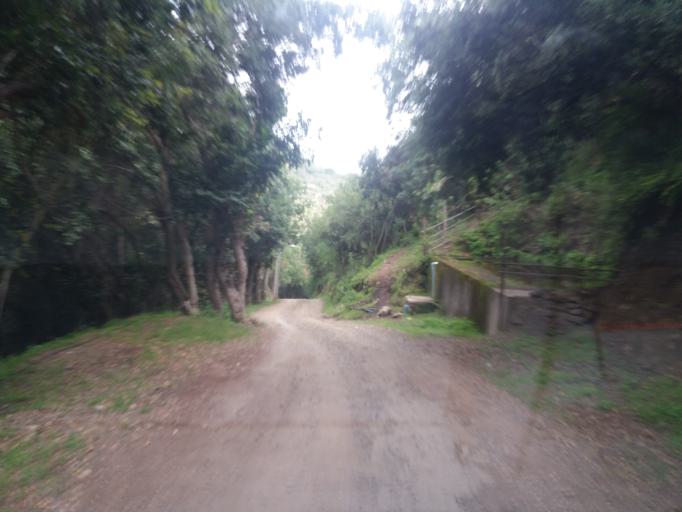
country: CL
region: Valparaiso
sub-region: Provincia de Marga Marga
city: Limache
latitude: -33.0766
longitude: -71.0608
